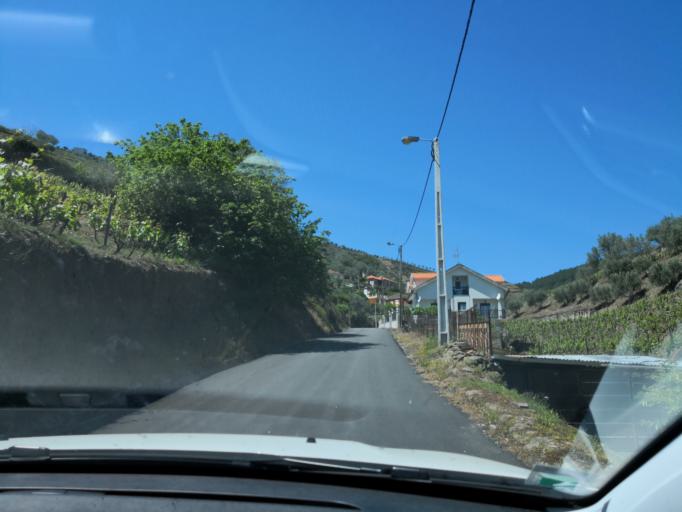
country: PT
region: Vila Real
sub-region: Vila Real
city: Vila Real
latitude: 41.2284
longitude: -7.7224
